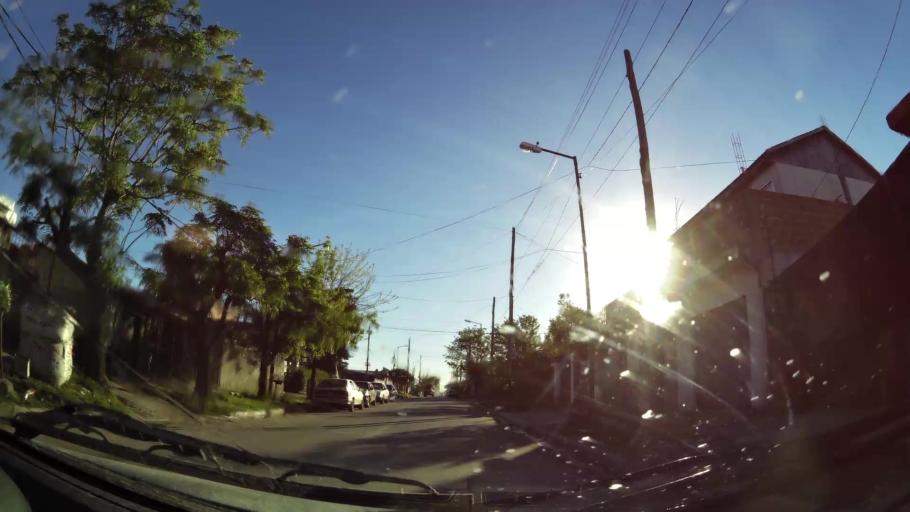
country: AR
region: Buenos Aires
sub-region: Partido de Almirante Brown
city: Adrogue
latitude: -34.7685
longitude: -58.3372
